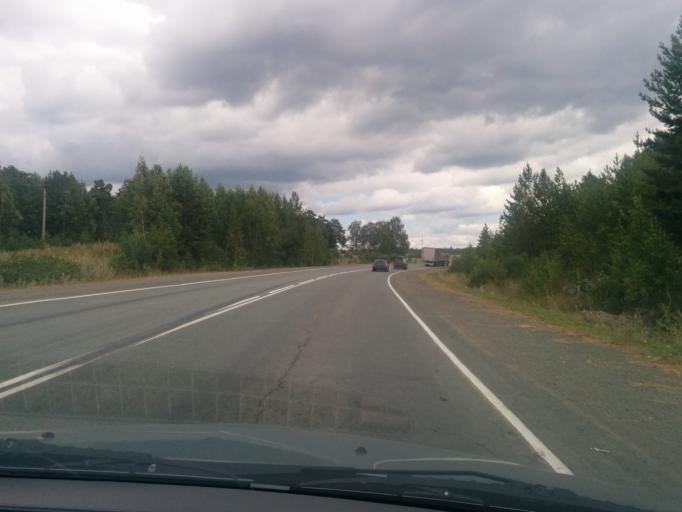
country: RU
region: Bashkortostan
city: Lomovka
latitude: 53.8961
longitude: 58.0895
